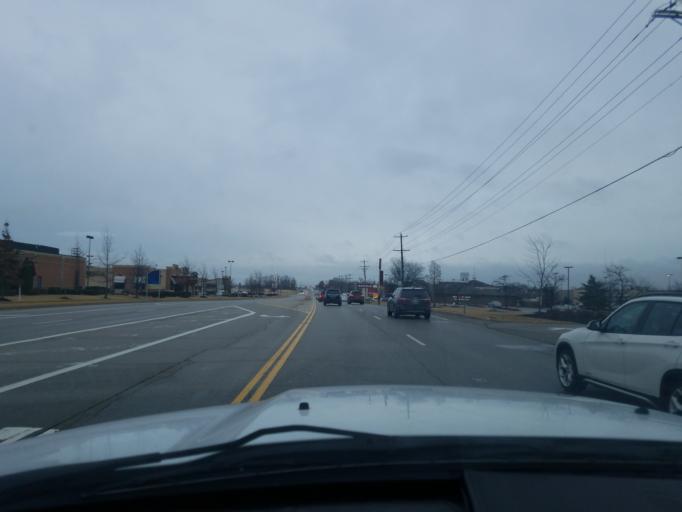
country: US
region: Ohio
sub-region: Butler County
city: Wetherington
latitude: 39.3528
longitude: -84.3640
